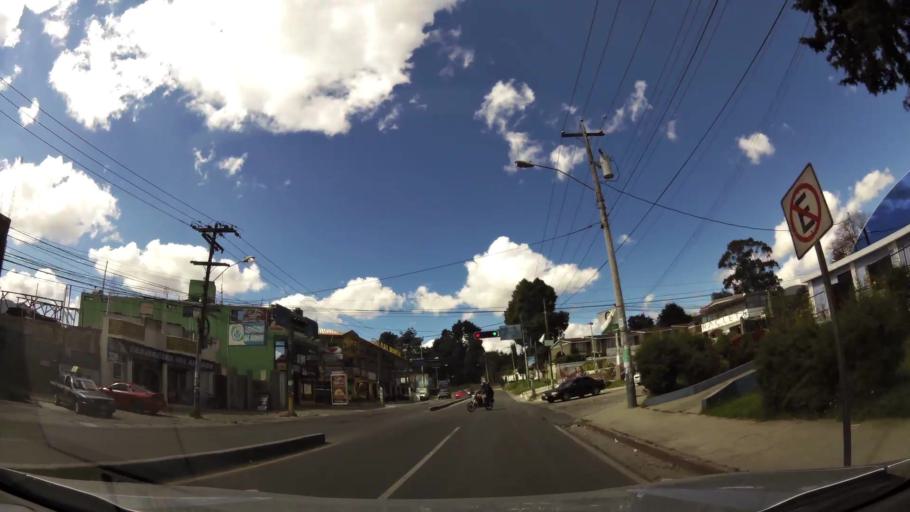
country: GT
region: Quetzaltenango
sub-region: Municipio de La Esperanza
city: La Esperanza
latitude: 14.8580
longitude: -91.5406
